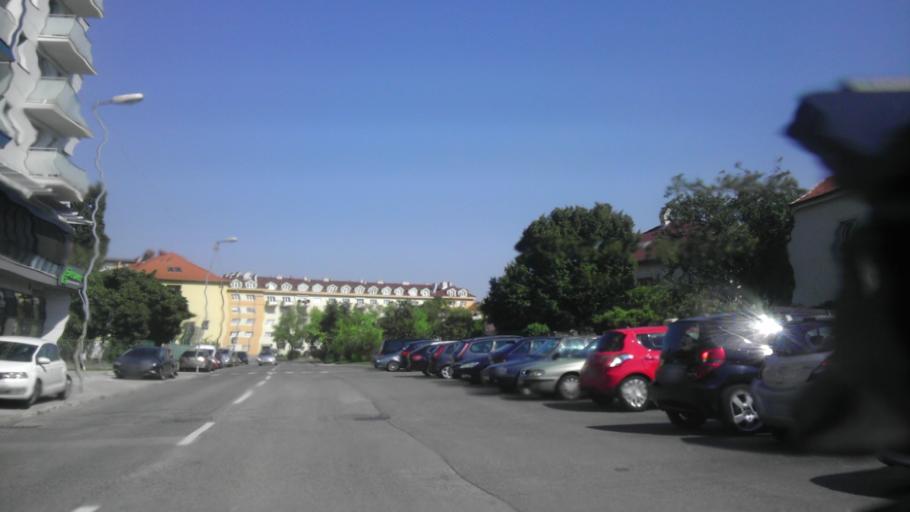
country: SK
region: Bratislavsky
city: Bratislava
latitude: 48.1705
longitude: 17.1315
